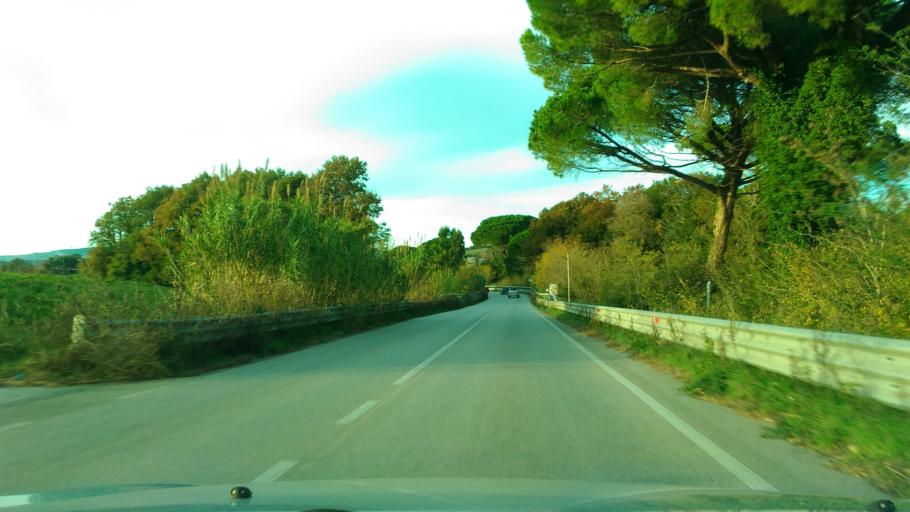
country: IT
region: Tuscany
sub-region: Provincia di Livorno
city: S.P. in Palazzi
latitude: 43.3703
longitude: 10.5058
